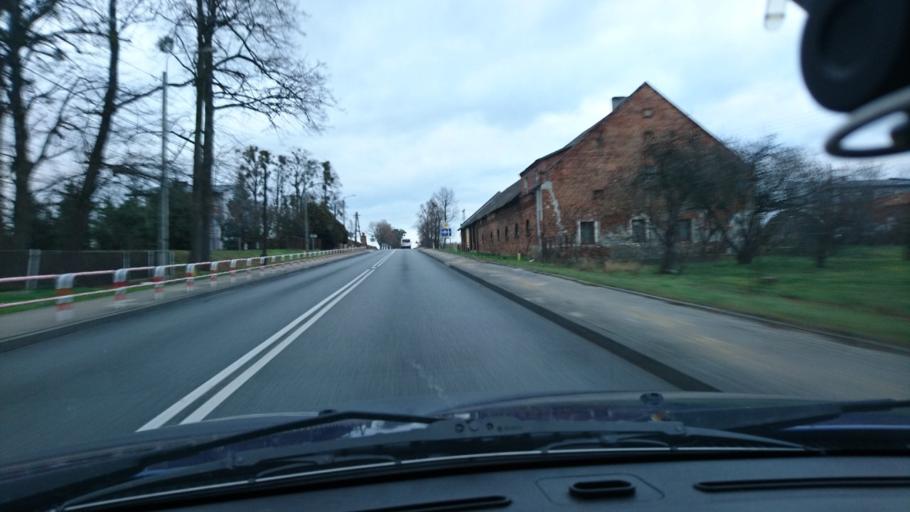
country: PL
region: Opole Voivodeship
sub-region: Powiat kluczborski
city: Kluczbork
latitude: 51.0288
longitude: 18.1921
